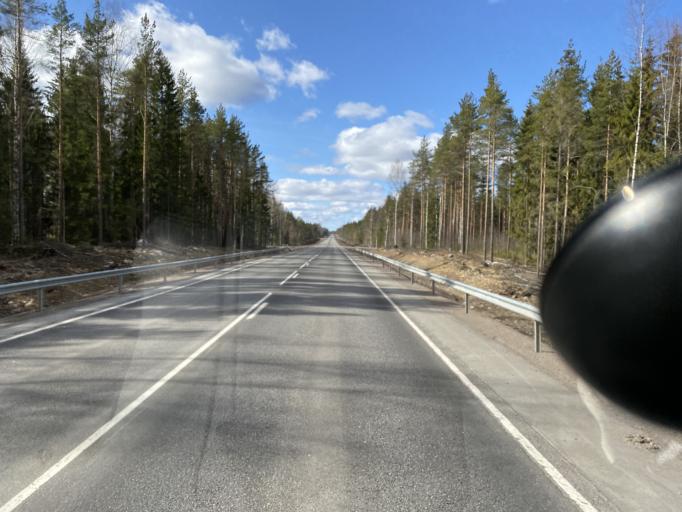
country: FI
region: Satakunta
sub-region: Pori
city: Huittinen
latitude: 61.1746
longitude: 22.5617
